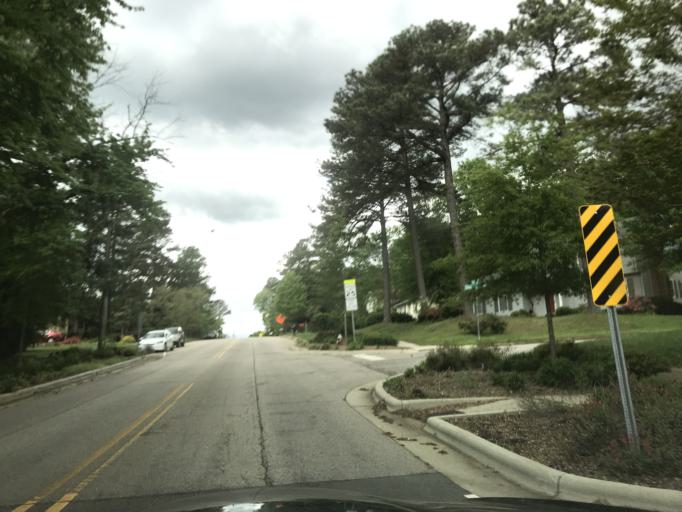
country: US
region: North Carolina
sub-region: Wake County
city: West Raleigh
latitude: 35.7772
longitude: -78.7016
